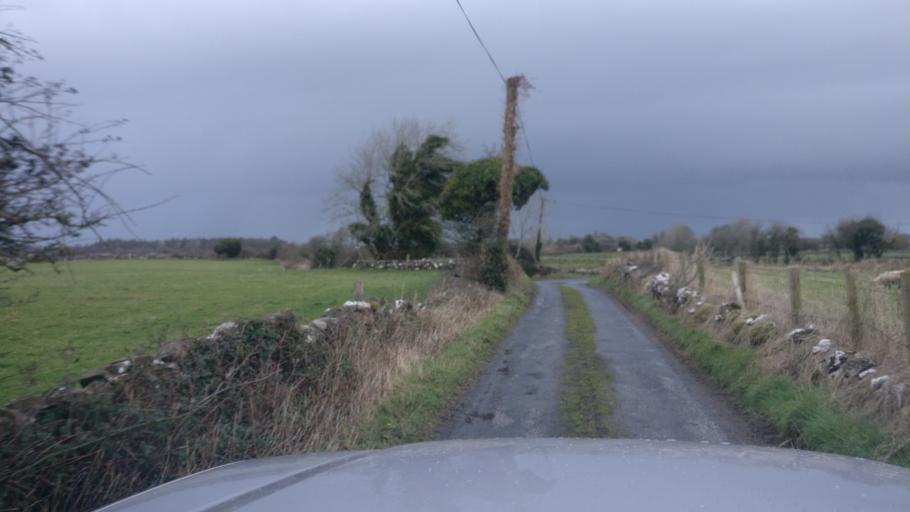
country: IE
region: Connaught
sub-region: County Galway
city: Loughrea
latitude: 53.2010
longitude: -8.6133
